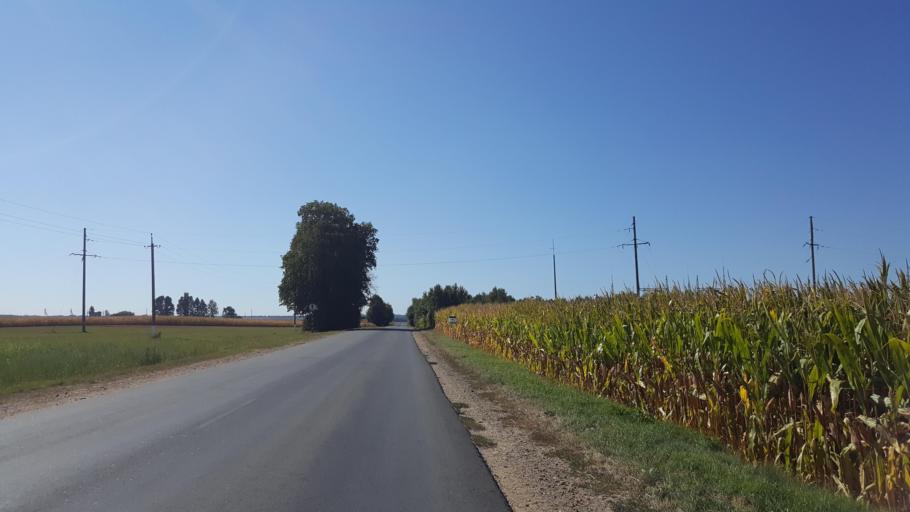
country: BY
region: Brest
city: Charnawchytsy
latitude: 52.2870
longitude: 23.6044
